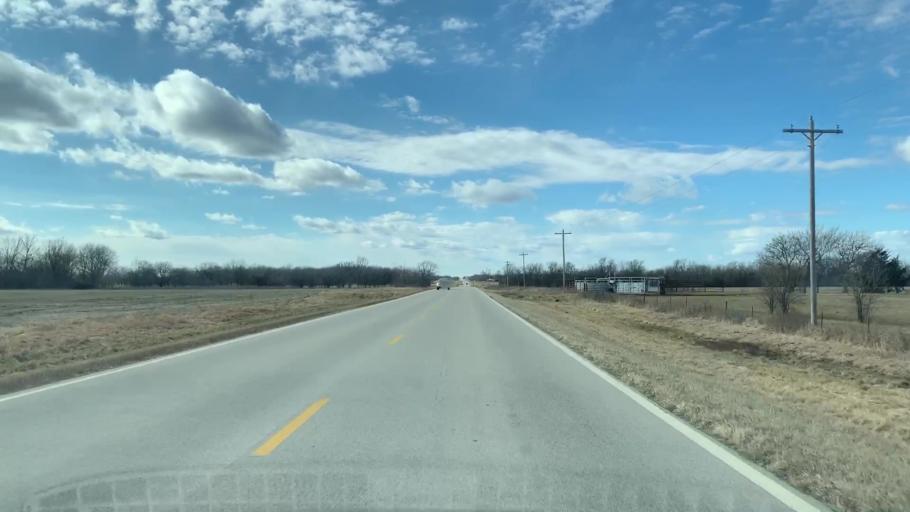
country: US
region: Kansas
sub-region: Neosho County
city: Chanute
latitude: 37.5292
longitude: -95.4014
